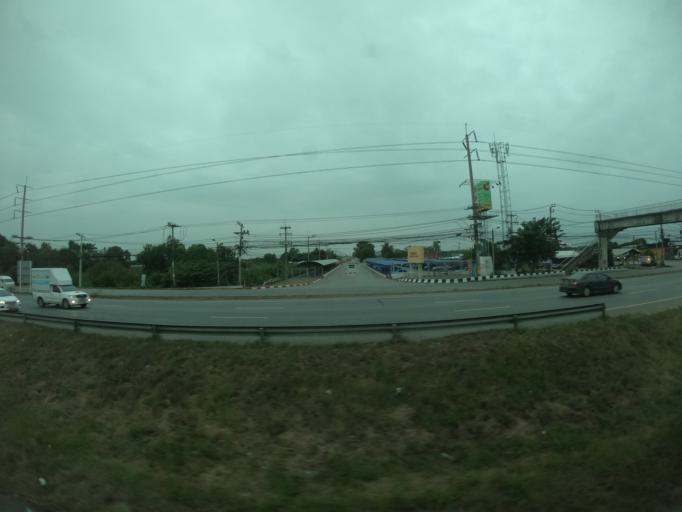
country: TH
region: Phra Nakhon Si Ayutthaya
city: Wang Noi
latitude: 14.2083
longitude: 100.6709
